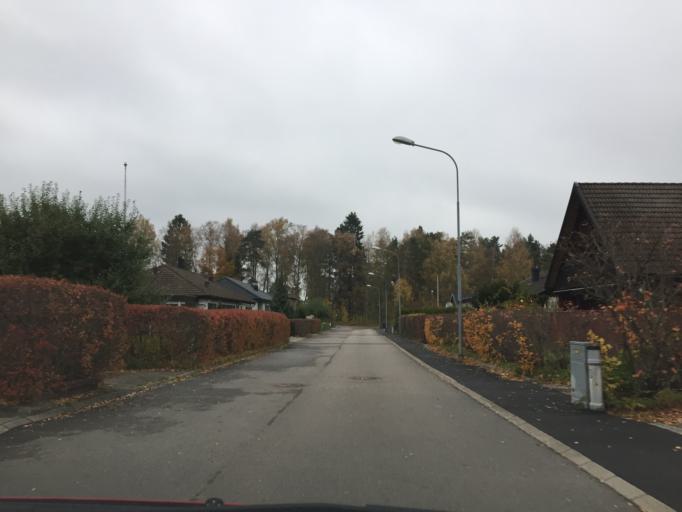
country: SE
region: Vaestra Goetaland
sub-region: Trollhattan
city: Trollhattan
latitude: 58.2570
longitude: 12.2903
